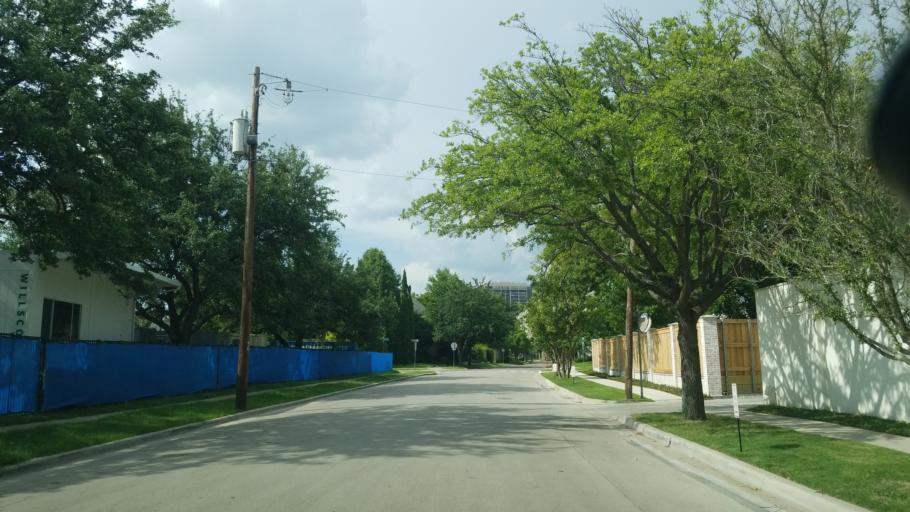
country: US
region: Texas
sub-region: Dallas County
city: University Park
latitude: 32.8596
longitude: -96.7994
